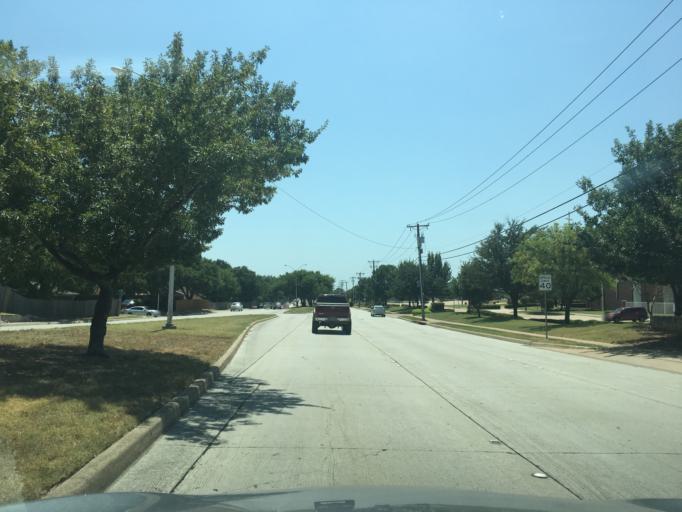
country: US
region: Texas
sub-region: Tarrant County
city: Edgecliff Village
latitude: 32.6313
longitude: -97.3699
